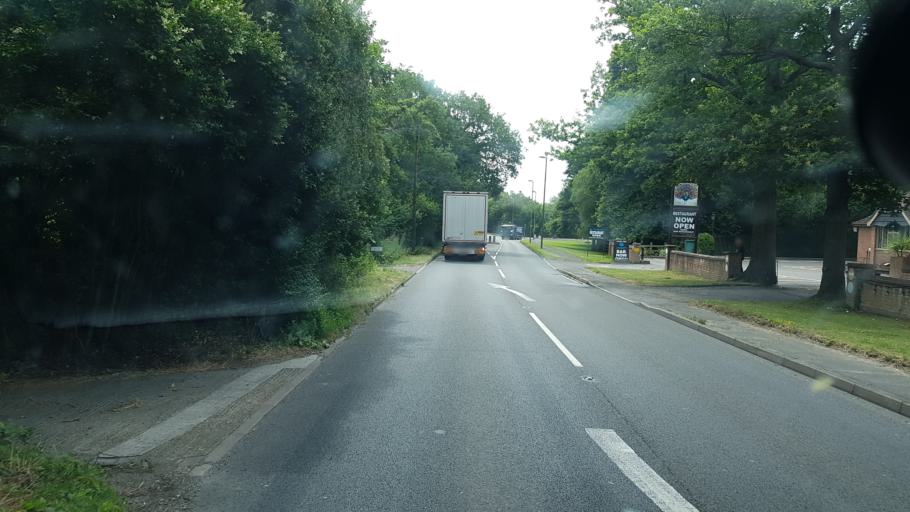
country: GB
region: England
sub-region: Surrey
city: Felbridge
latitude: 51.1567
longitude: -0.0506
